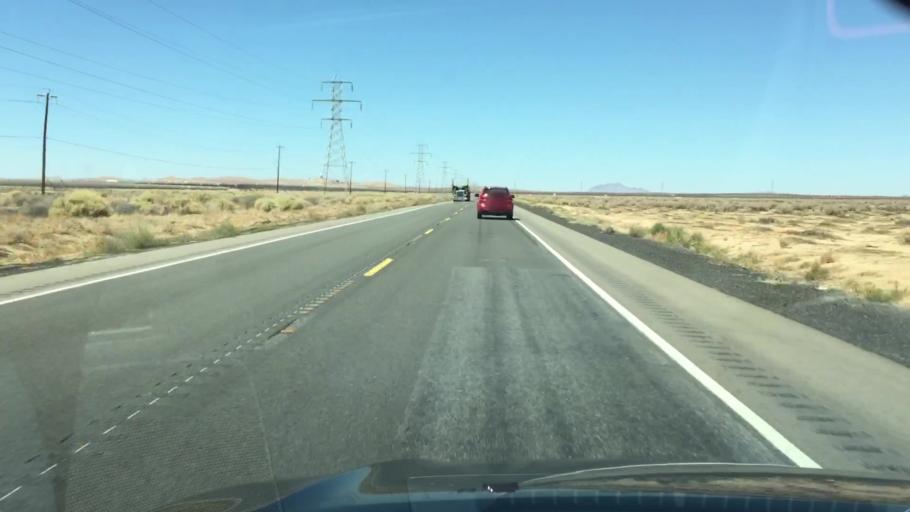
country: US
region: California
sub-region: Kern County
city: Boron
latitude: 35.0155
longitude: -117.5480
